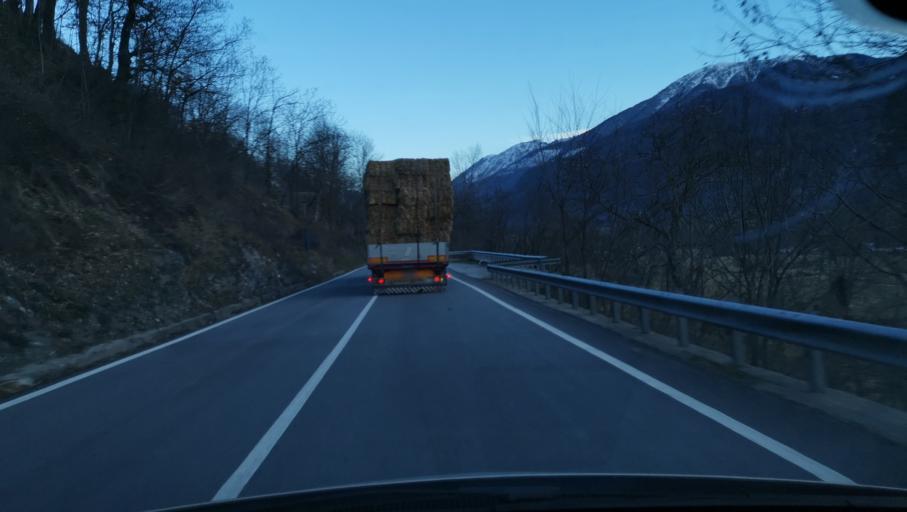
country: IT
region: Piedmont
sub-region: Provincia di Cuneo
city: Demonte
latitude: 44.3164
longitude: 7.2667
